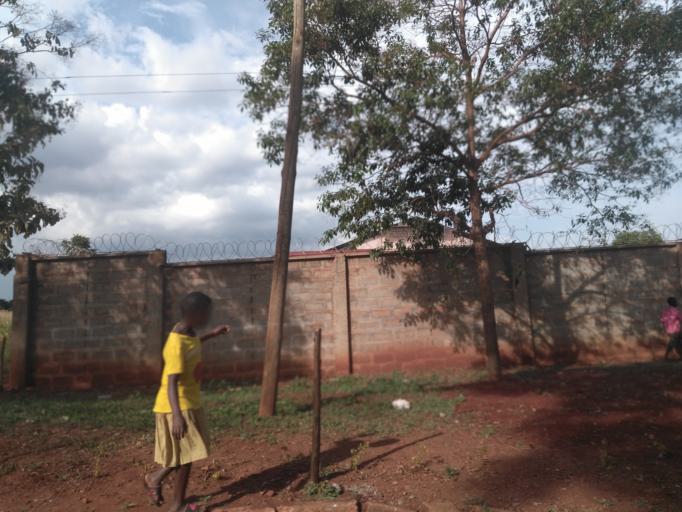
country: UG
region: Eastern Region
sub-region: Jinja District
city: Jinja
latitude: 0.4200
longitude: 33.2128
